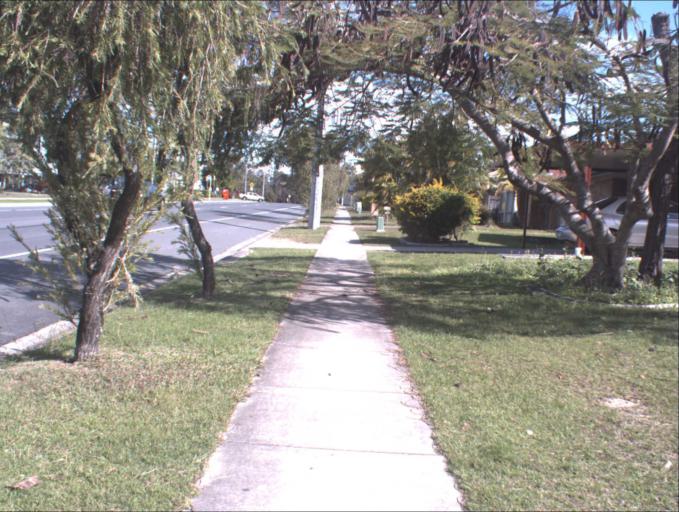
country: AU
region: Queensland
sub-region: Logan
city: Logan Reserve
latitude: -27.6956
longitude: 153.0821
